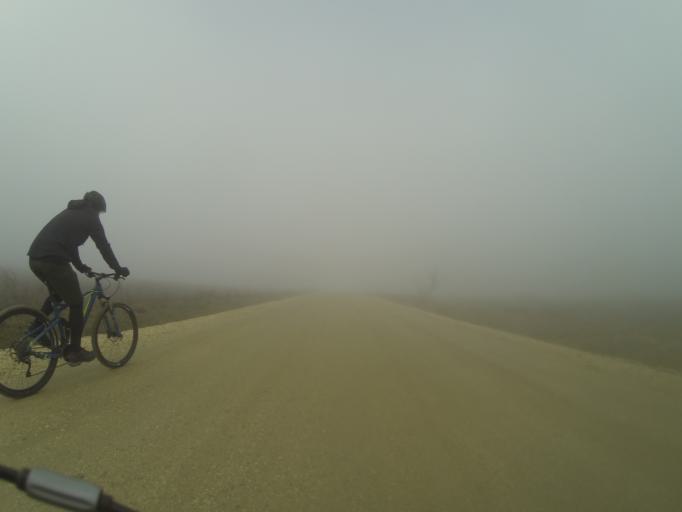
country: RO
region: Mehedinti
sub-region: Comuna Baclesu
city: Baclesu
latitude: 44.4460
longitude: 23.1275
